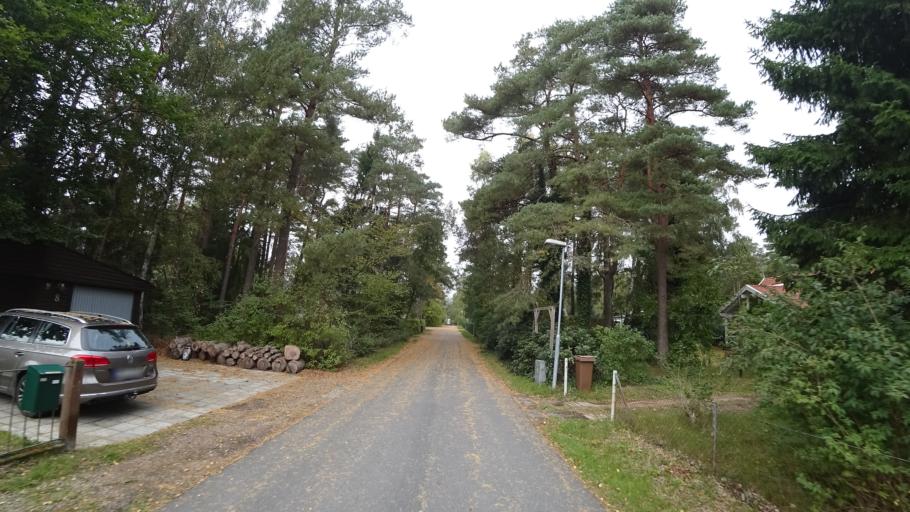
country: SE
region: Skane
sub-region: Kavlinge Kommun
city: Hofterup
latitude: 55.8010
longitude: 12.9894
